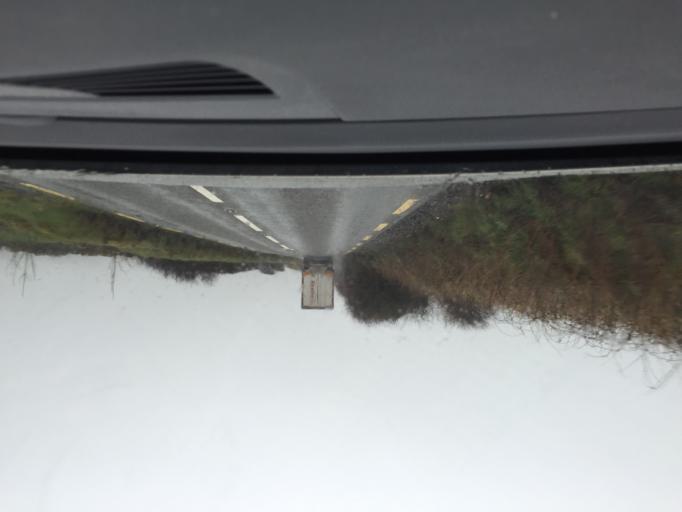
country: IE
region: Munster
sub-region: Ciarrai
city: Dingle
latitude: 52.1428
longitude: -10.1129
